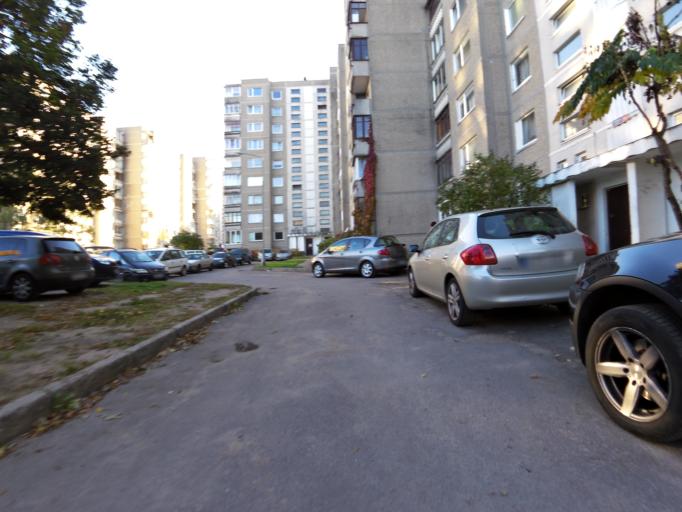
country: LT
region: Vilnius County
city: Justiniskes
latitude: 54.7227
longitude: 25.2143
